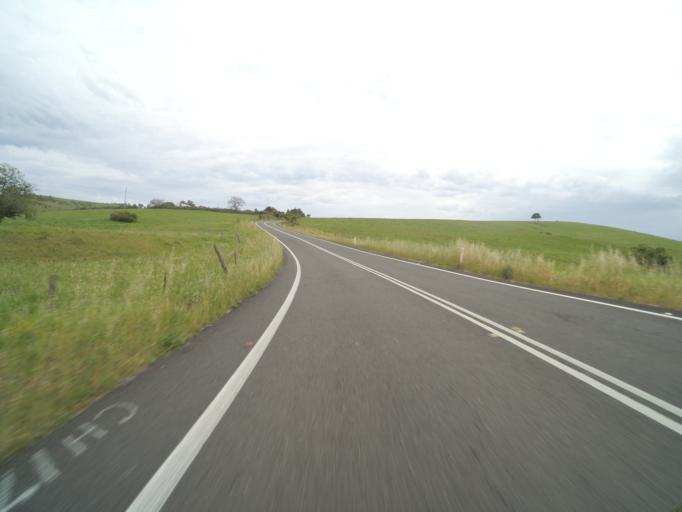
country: AU
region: New South Wales
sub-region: Kiama
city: Kiama
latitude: -34.6587
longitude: 150.8186
